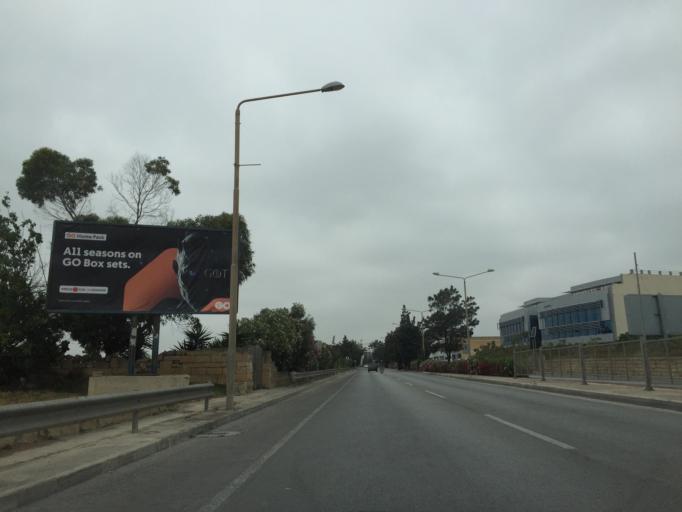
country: MT
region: Saint Venera
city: Santa Venera
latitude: 35.8862
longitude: 14.4681
